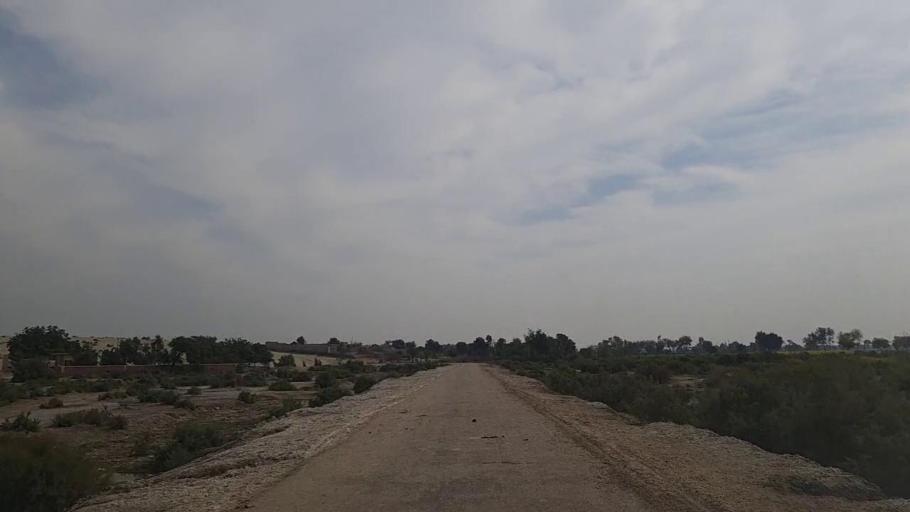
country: PK
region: Sindh
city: Daur
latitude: 26.4292
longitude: 68.4717
